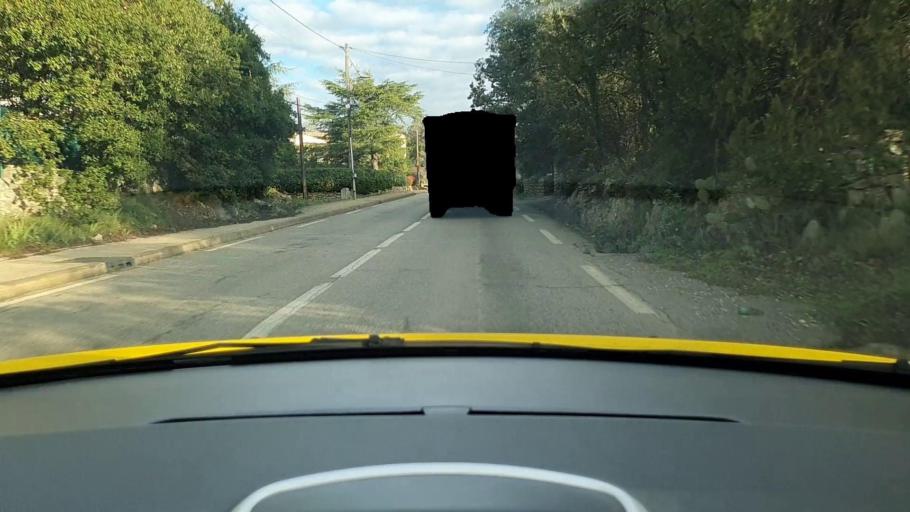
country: FR
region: Languedoc-Roussillon
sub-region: Departement du Gard
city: Saint-Martin-de-Valgalgues
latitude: 44.1843
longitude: 4.0813
